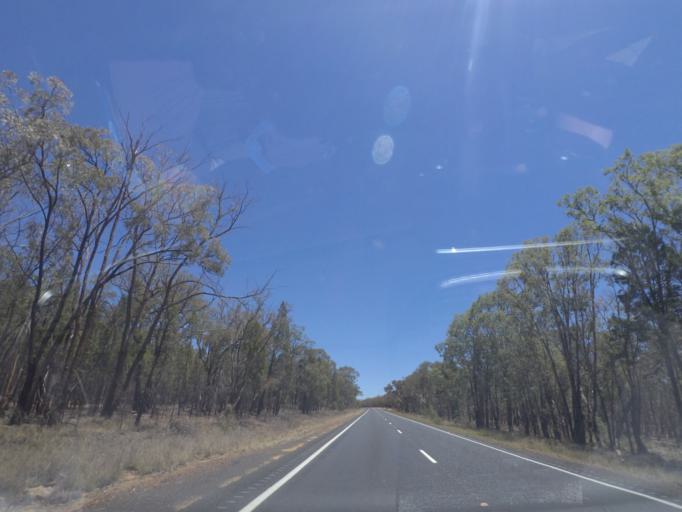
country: AU
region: New South Wales
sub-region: Warrumbungle Shire
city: Coonabarabran
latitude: -31.2020
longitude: 149.3407
